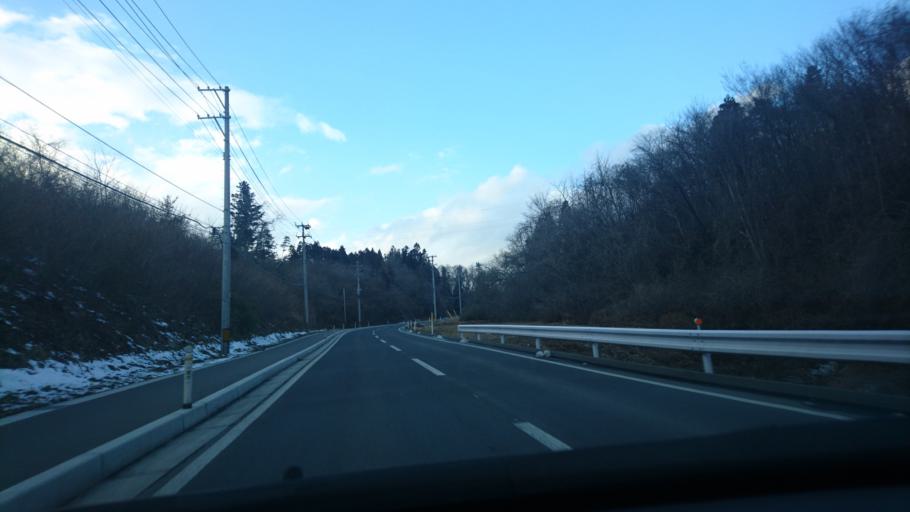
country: JP
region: Iwate
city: Ichinoseki
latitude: 39.0024
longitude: 141.3333
